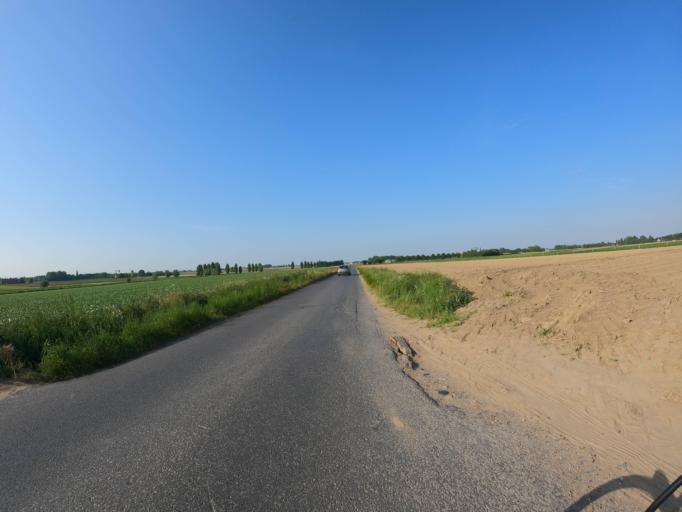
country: BE
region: Flanders
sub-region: Provincie West-Vlaanderen
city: Tielt
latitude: 51.0086
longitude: 3.3401
